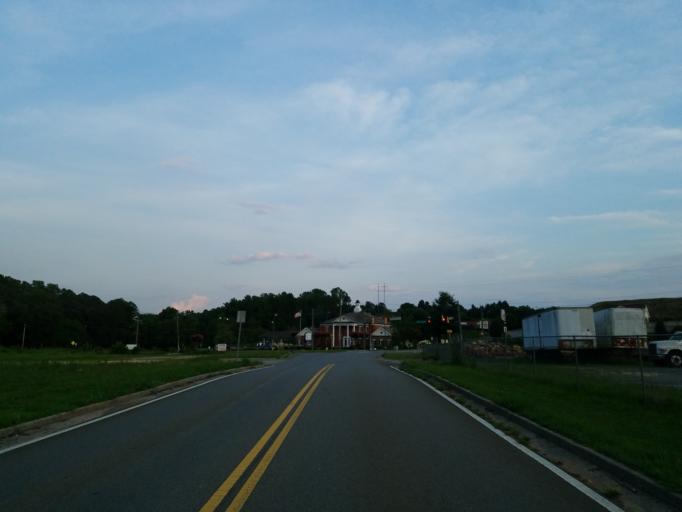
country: US
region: Georgia
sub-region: Pickens County
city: Jasper
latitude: 34.4666
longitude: -84.4509
